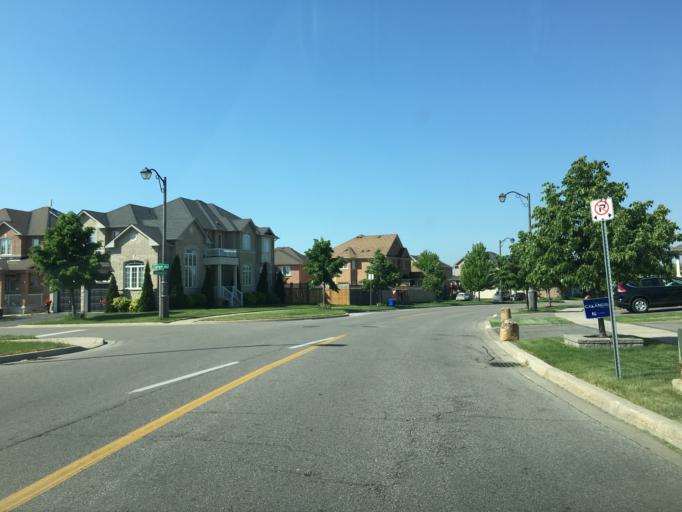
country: CA
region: Ontario
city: Markham
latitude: 43.8576
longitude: -79.2219
